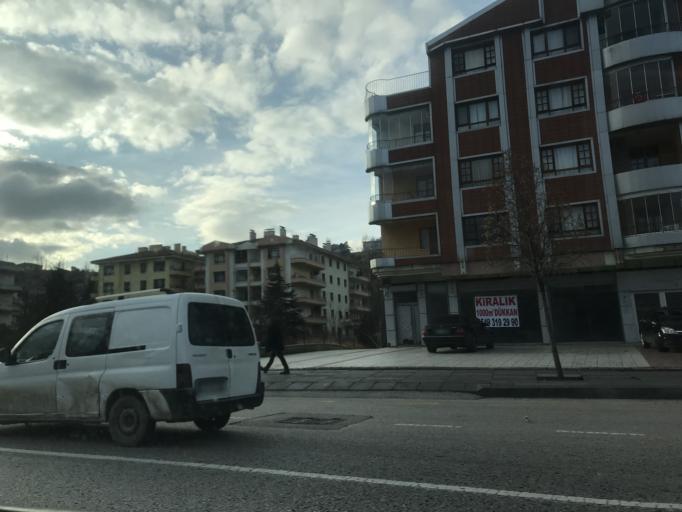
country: TR
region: Ankara
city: Mamak
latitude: 39.9878
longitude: 32.8974
